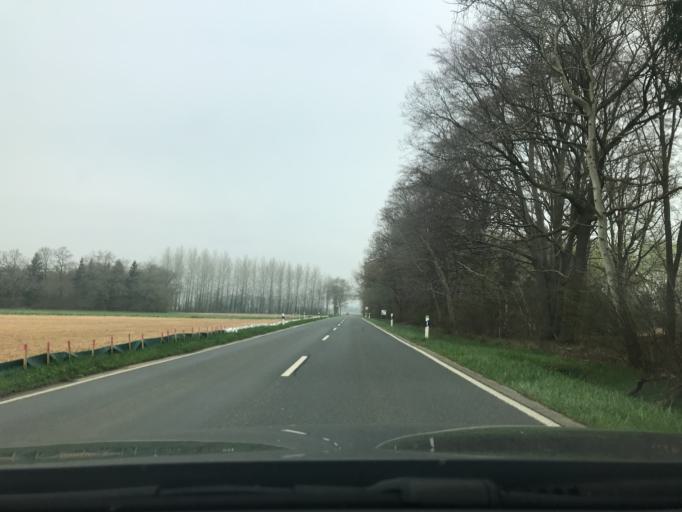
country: DE
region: North Rhine-Westphalia
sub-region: Regierungsbezirk Dusseldorf
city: Wachtendonk
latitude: 51.4618
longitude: 6.3297
